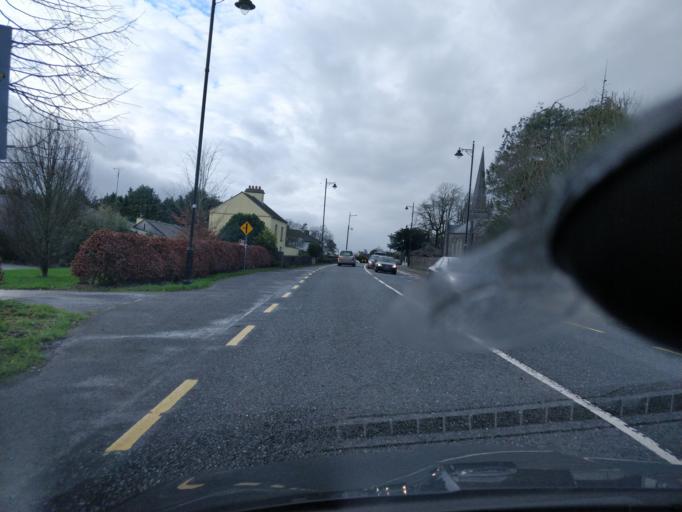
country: IE
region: Connaught
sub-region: Roscommon
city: Roscommon
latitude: 53.7767
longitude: -8.1093
